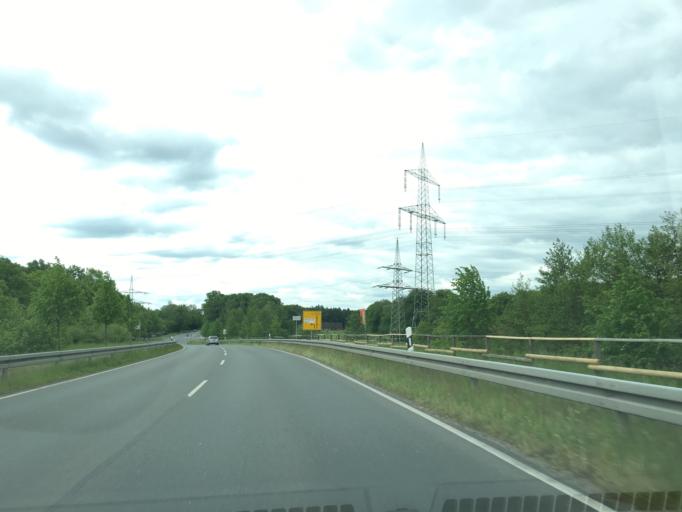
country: DE
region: North Rhine-Westphalia
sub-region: Regierungsbezirk Munster
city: Muenster
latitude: 51.8884
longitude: 7.6469
